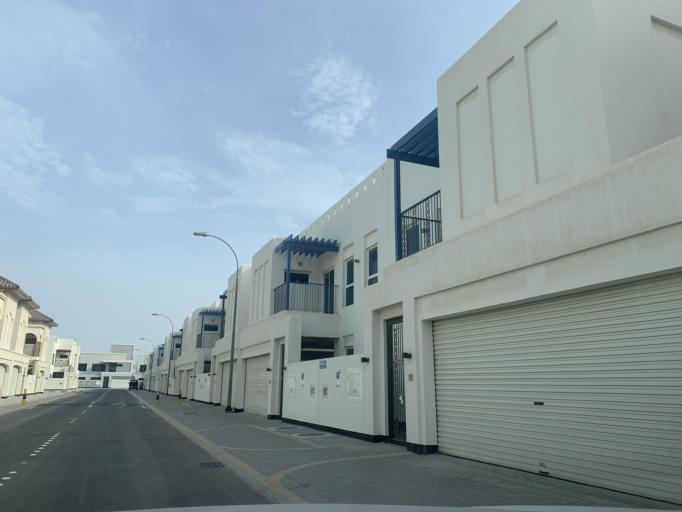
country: BH
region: Muharraq
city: Al Muharraq
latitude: 26.3182
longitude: 50.6282
